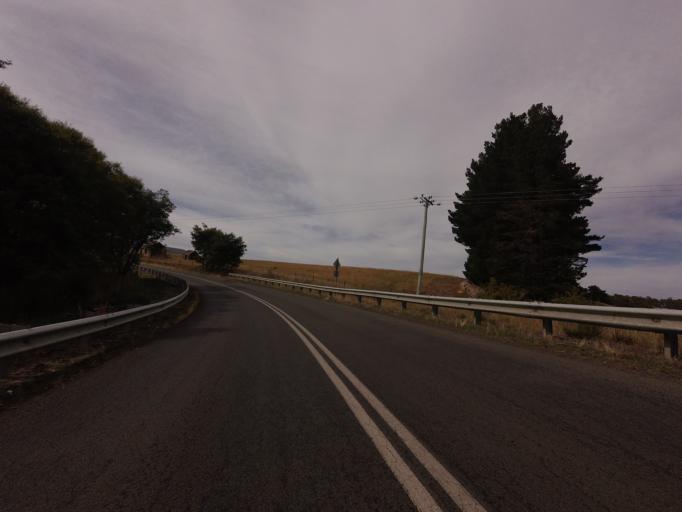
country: AU
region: Tasmania
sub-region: Sorell
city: Sorell
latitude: -42.4302
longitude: 147.4658
